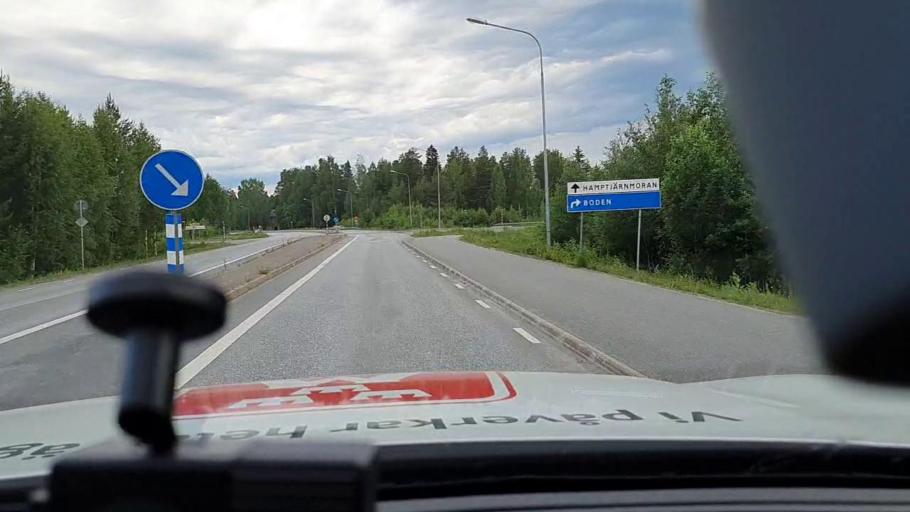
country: SE
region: Norrbotten
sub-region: Bodens Kommun
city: Boden
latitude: 65.8136
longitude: 21.6491
